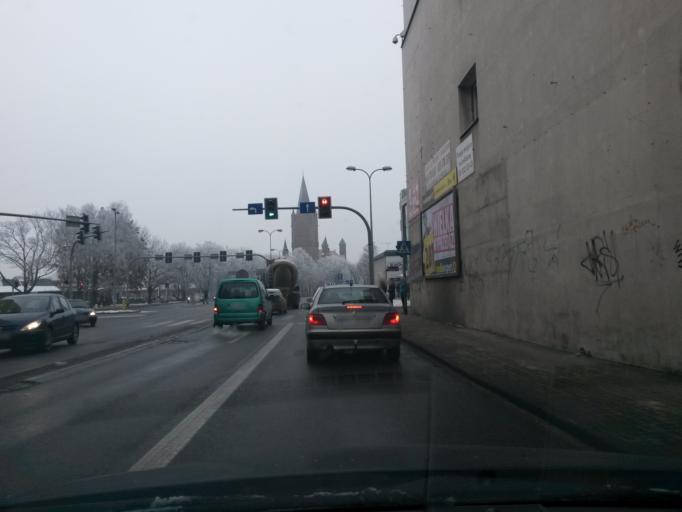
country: PL
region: Kujawsko-Pomorskie
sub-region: Powiat inowroclawski
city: Inowroclaw
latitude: 52.7990
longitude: 18.2555
